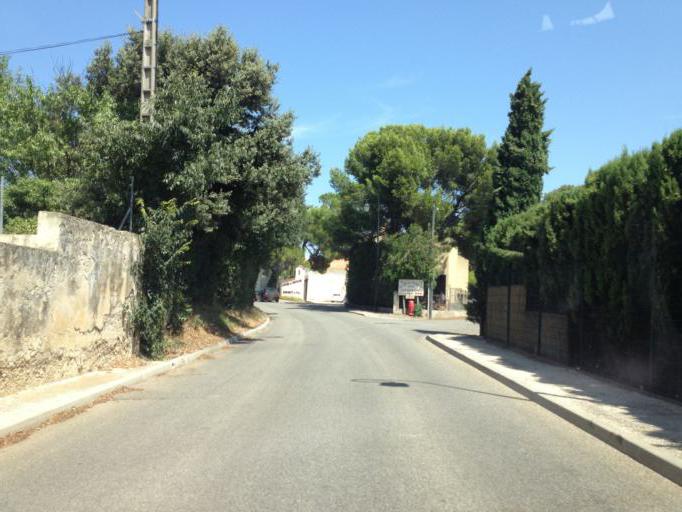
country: FR
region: Provence-Alpes-Cote d'Azur
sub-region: Departement du Vaucluse
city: Chateauneuf-du-Pape
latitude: 44.0595
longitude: 4.8368
